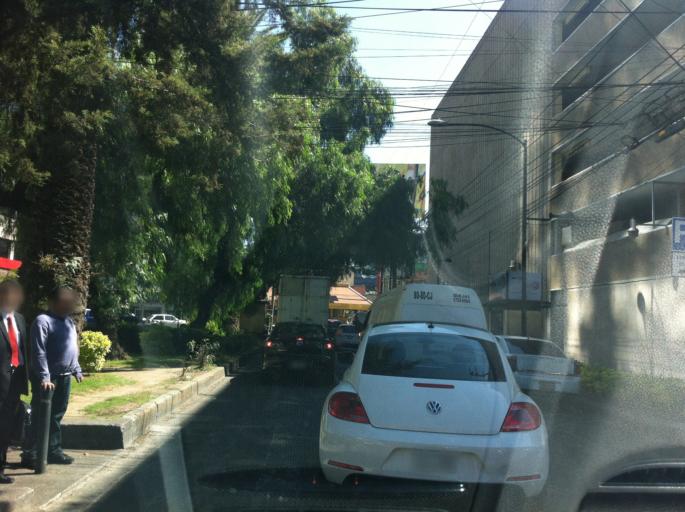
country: MX
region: Mexico City
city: Miguel Hidalgo
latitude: 19.4353
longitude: -99.1835
